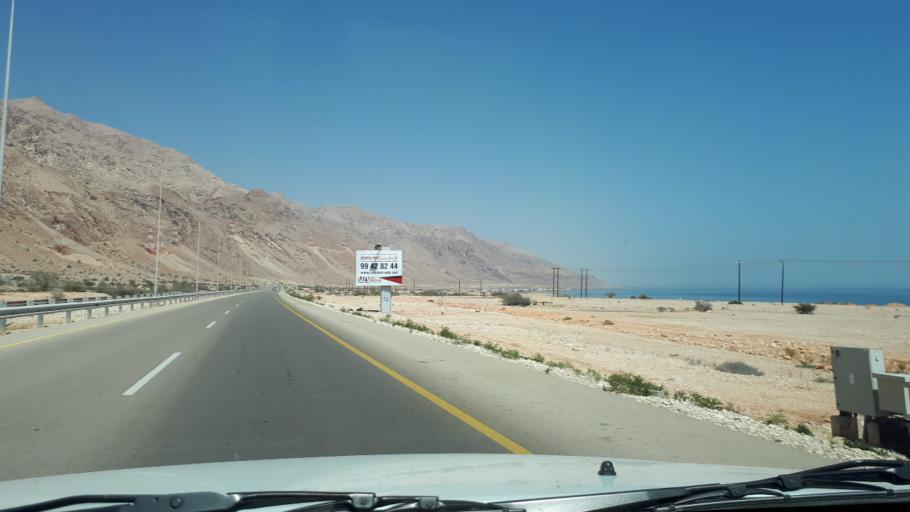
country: OM
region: Ash Sharqiyah
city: Sur
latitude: 22.7520
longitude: 59.3069
